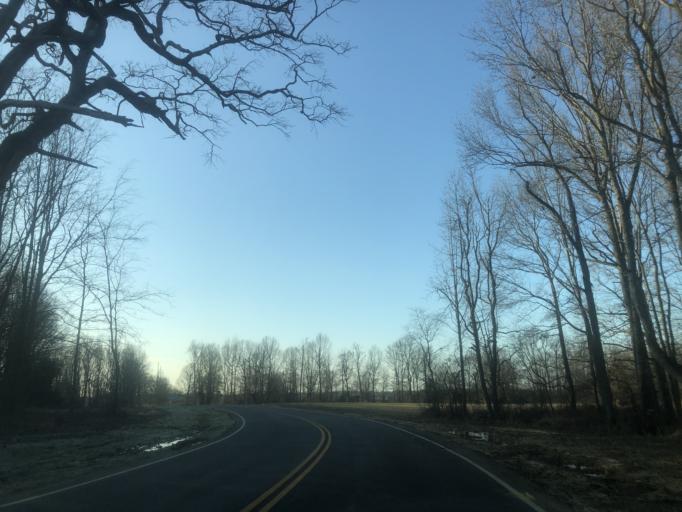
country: US
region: Tennessee
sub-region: Sumner County
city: White House
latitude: 36.4812
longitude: -86.6948
